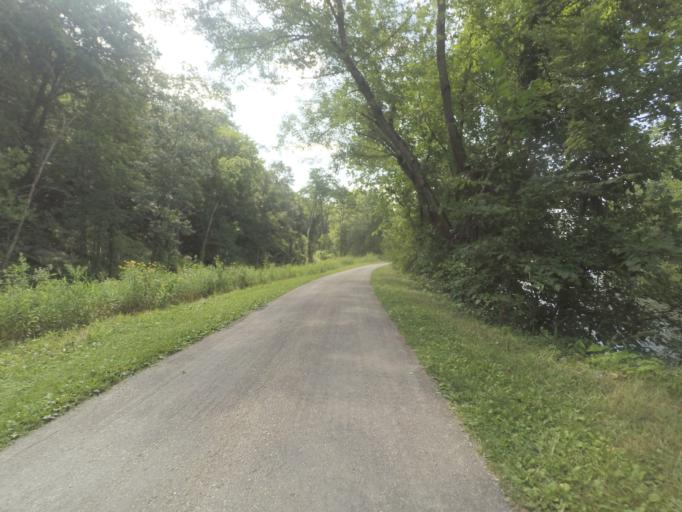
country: US
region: Ohio
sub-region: Cuyahoga County
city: Brecksville
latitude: 41.3235
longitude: -81.5868
